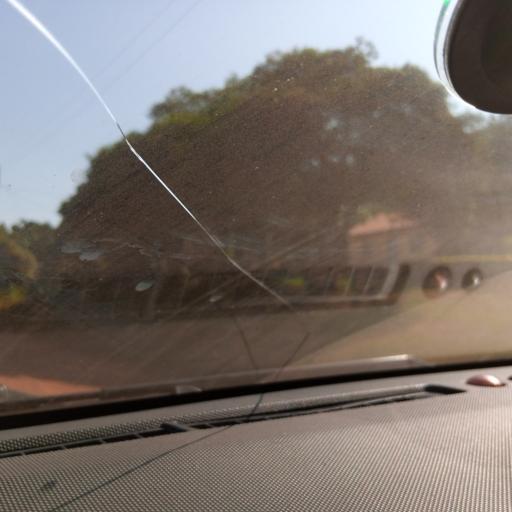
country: UG
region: Central Region
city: Masaka
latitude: -0.3394
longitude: 31.7325
